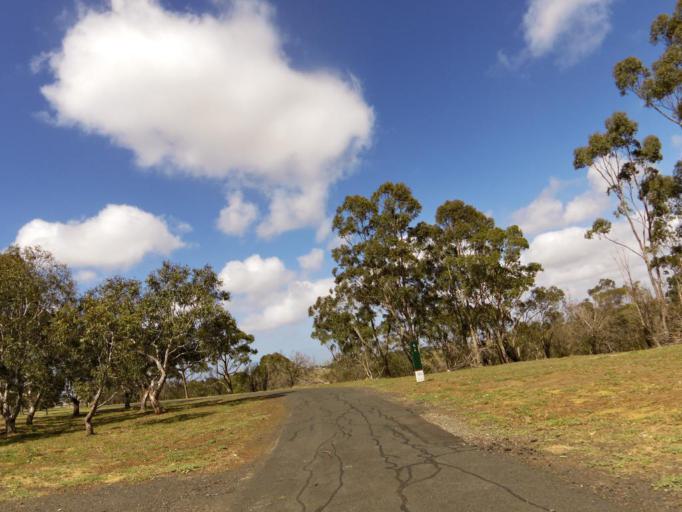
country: AU
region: Victoria
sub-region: Brimbank
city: Keilor Park
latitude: -37.7272
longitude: 144.8491
